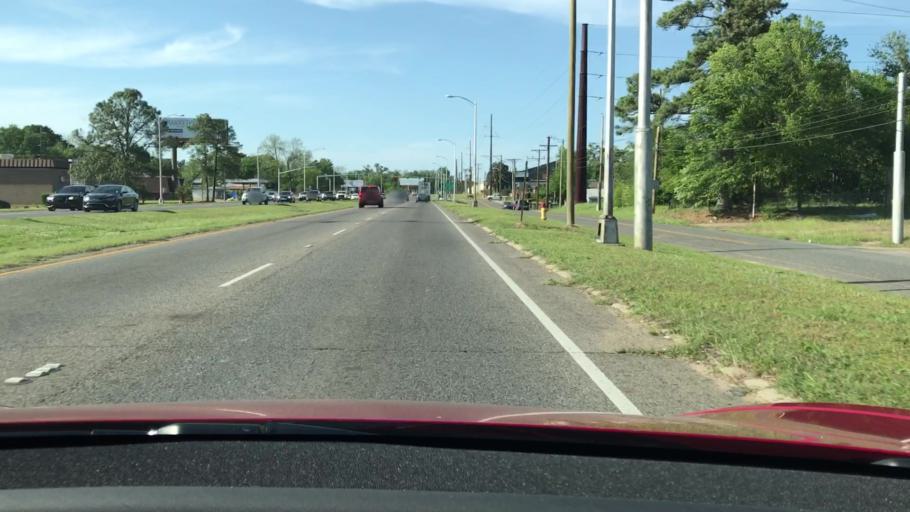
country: US
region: Louisiana
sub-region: Bossier Parish
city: Bossier City
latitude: 32.4980
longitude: -93.7248
